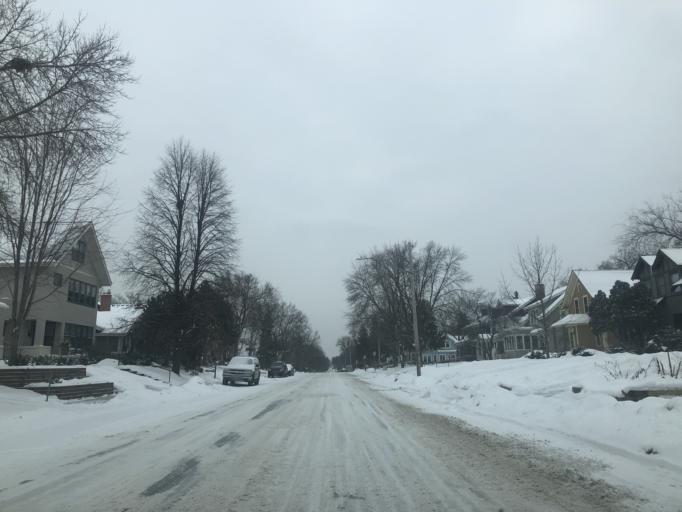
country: US
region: Minnesota
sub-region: Hennepin County
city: Richfield
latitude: 44.9296
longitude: -93.2909
